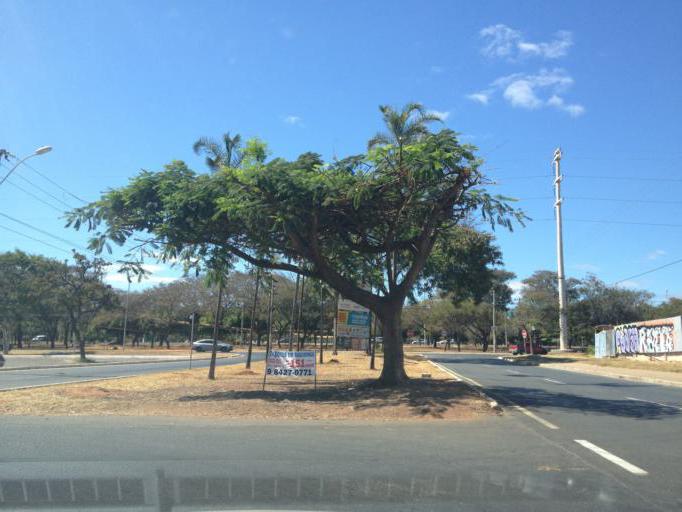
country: BR
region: Federal District
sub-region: Brasilia
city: Brasilia
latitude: -15.7962
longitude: -47.9464
